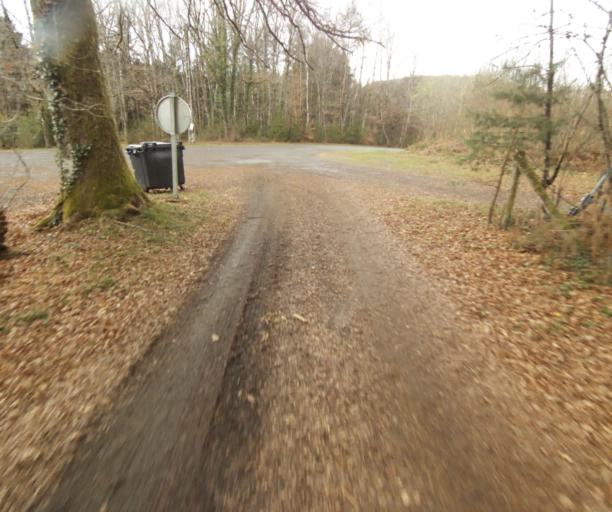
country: FR
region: Limousin
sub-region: Departement de la Correze
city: Saint-Privat
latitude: 45.2531
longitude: 1.9989
